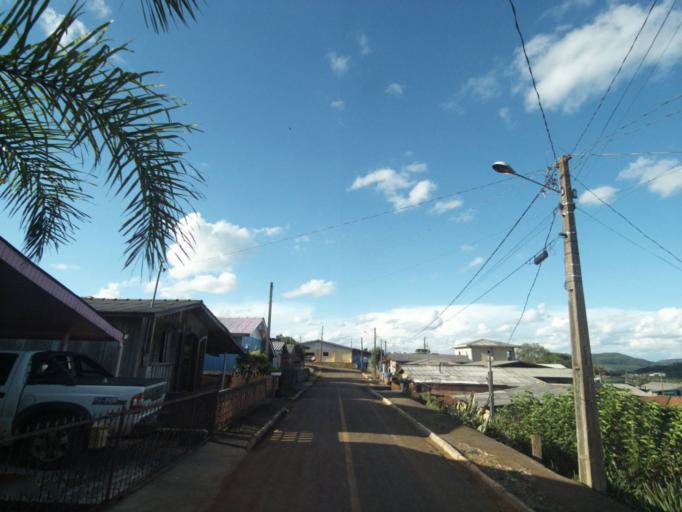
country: BR
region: Parana
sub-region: Uniao Da Vitoria
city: Uniao da Vitoria
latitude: -26.1671
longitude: -51.5377
